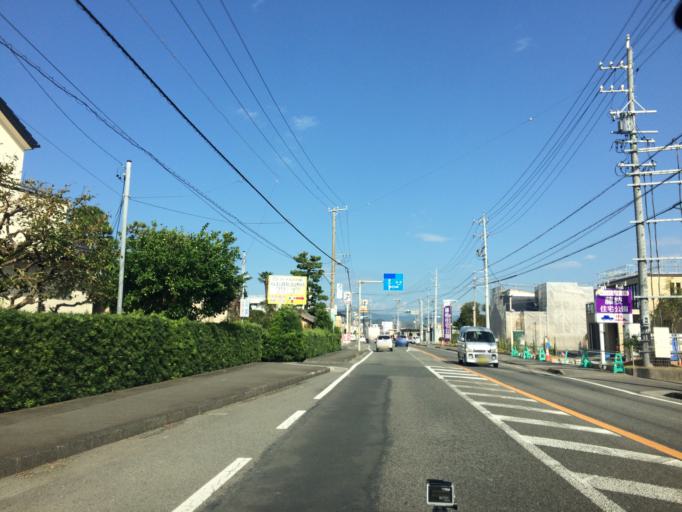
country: JP
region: Shizuoka
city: Fujieda
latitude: 34.8389
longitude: 138.2644
